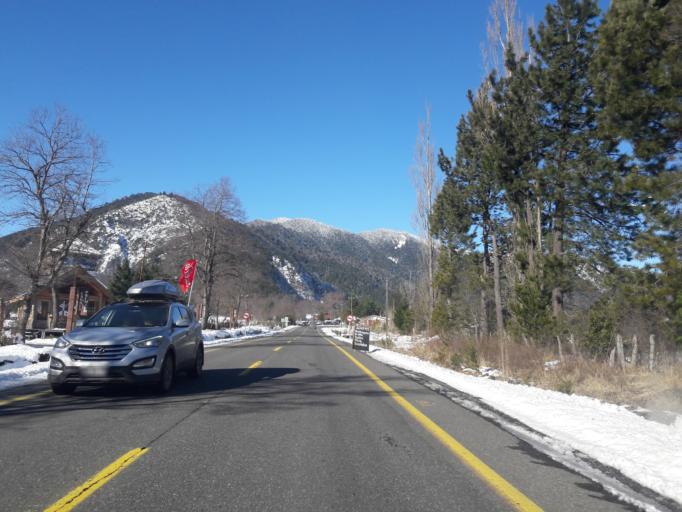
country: CL
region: Araucania
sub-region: Provincia de Cautin
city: Vilcun
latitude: -38.4780
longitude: -71.5393
